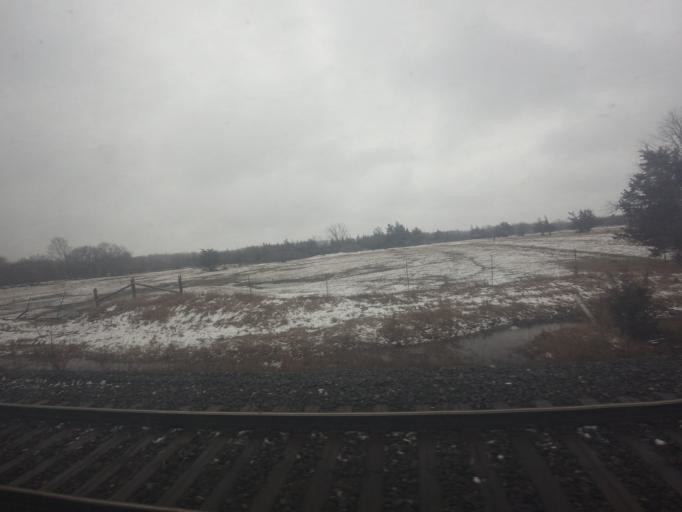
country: CA
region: Ontario
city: Belleville
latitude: 44.1972
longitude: -77.3038
